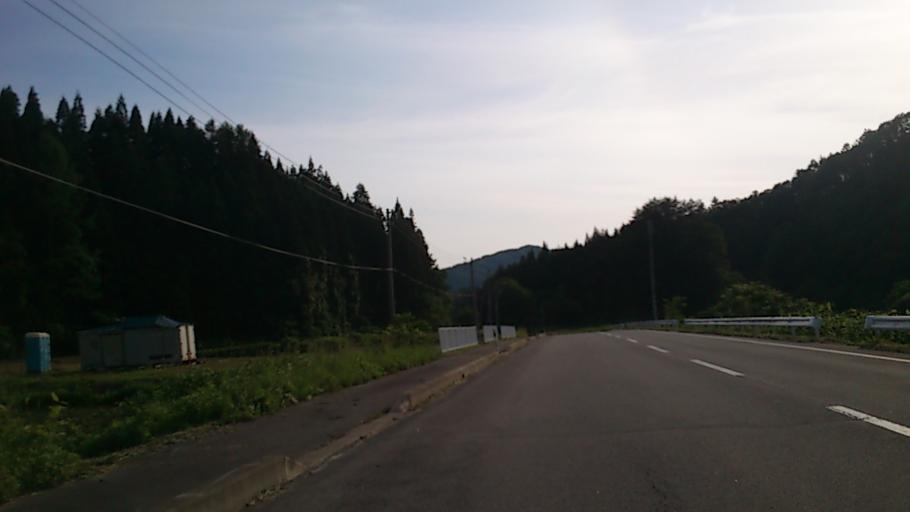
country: JP
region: Aomori
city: Kuroishi
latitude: 40.6272
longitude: 140.7072
